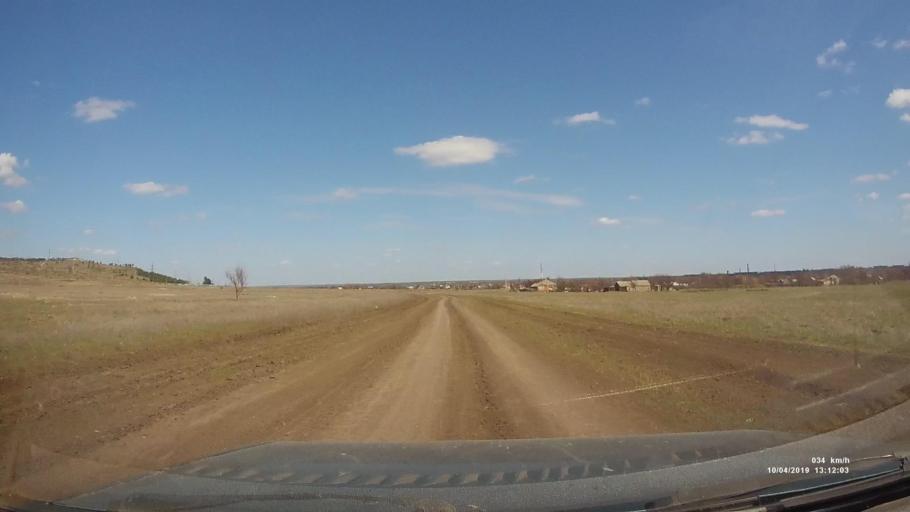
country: RU
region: Rostov
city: Masalovka
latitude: 48.4114
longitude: 40.2528
